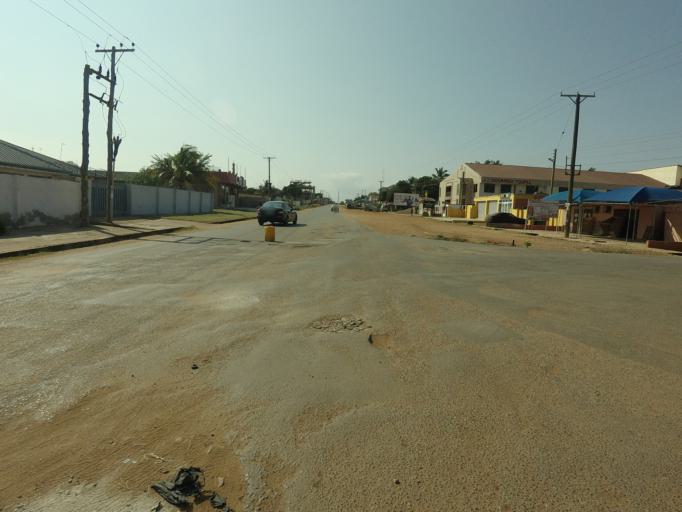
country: GH
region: Greater Accra
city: Teshi Old Town
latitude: 5.6018
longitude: -0.1040
